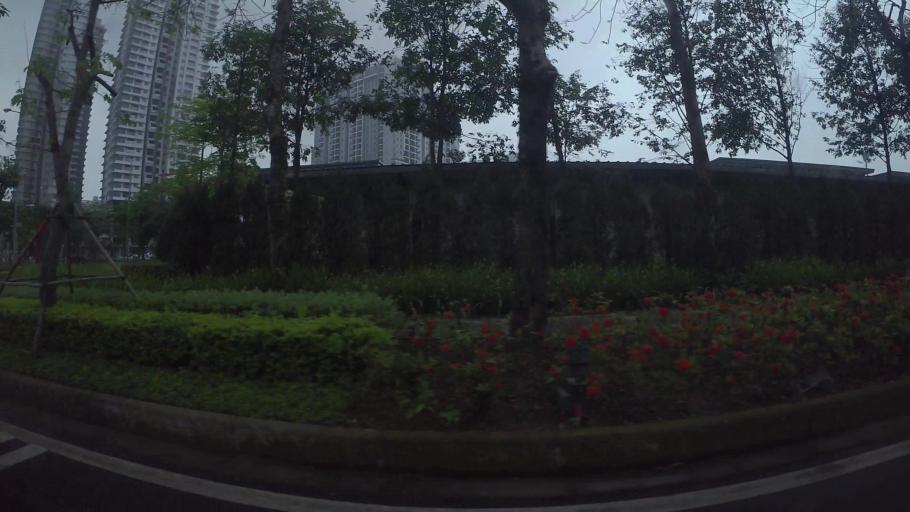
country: VN
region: Ha Noi
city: Van Dien
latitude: 20.9727
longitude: 105.8778
